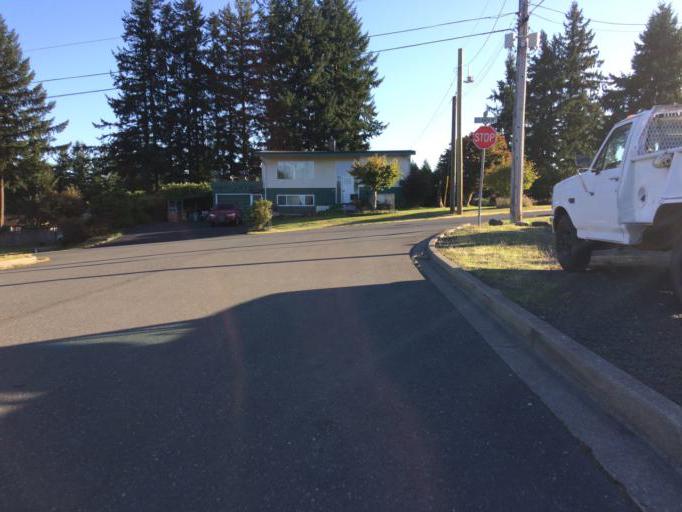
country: CA
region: British Columbia
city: Campbell River
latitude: 49.9856
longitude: -125.2309
